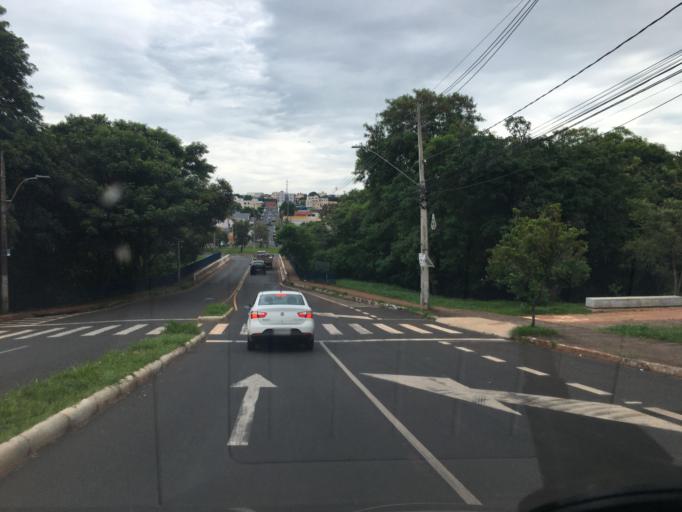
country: BR
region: Minas Gerais
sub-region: Uberlandia
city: Uberlandia
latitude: -18.9212
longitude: -48.3035
